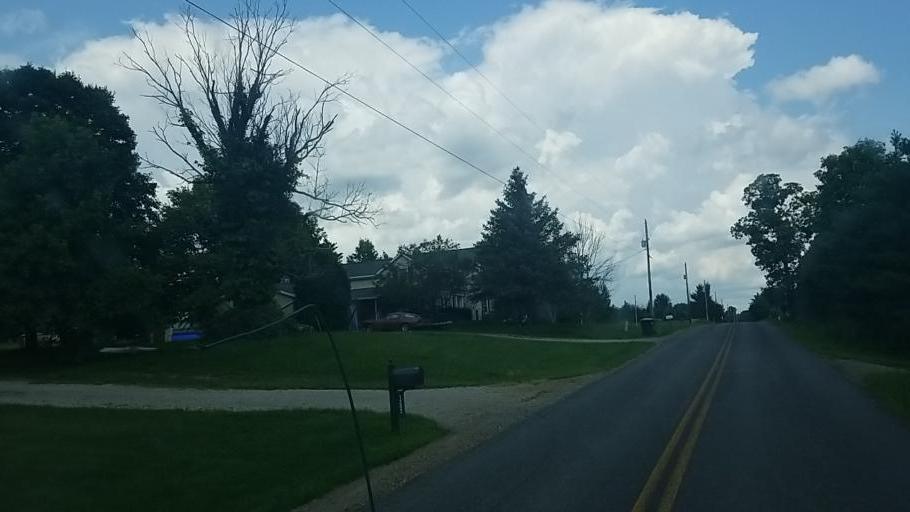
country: US
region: Ohio
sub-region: Medina County
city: Lodi
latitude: 41.0750
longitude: -82.0762
